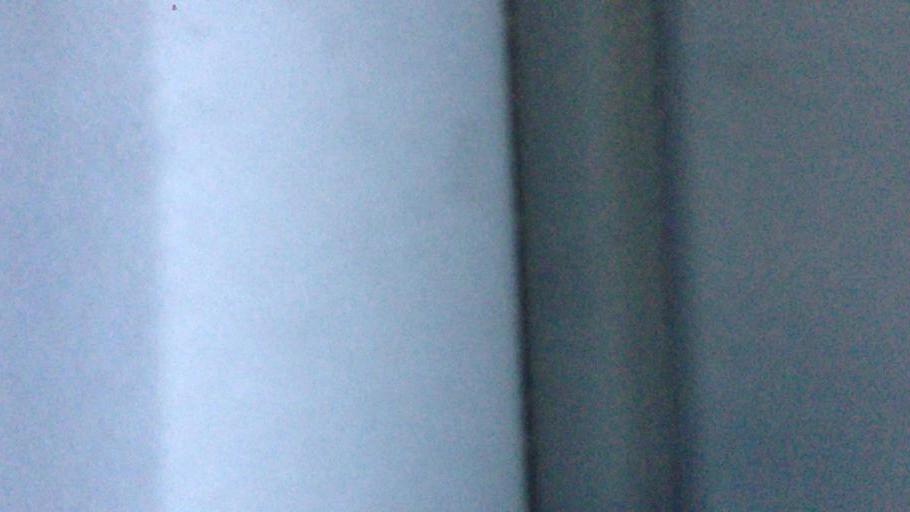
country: US
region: New York
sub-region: Dutchess County
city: Rhinebeck
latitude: 41.9571
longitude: -73.9199
